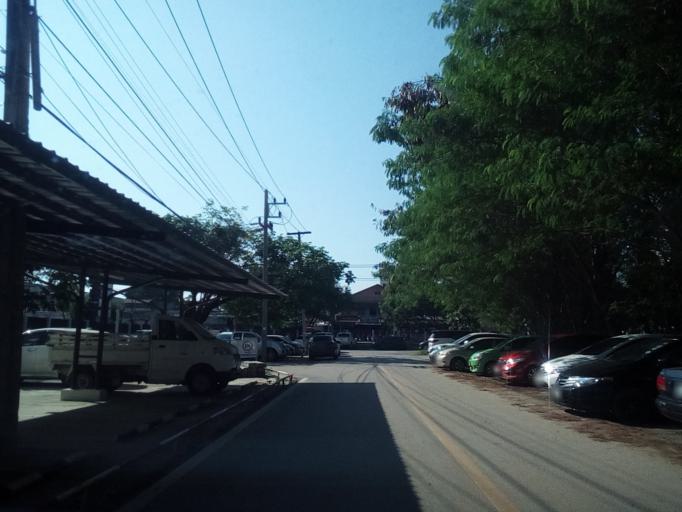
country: TH
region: Chiang Mai
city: Chiang Mai
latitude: 18.7930
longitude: 98.9572
